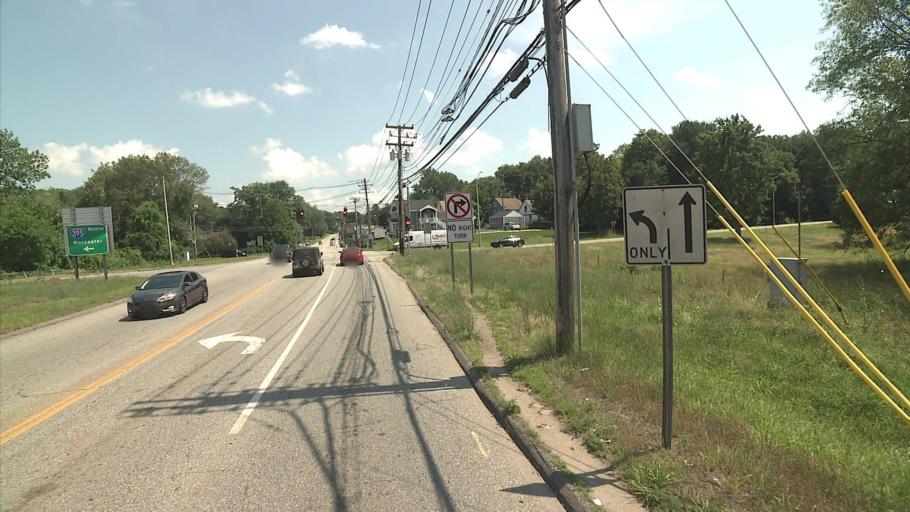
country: US
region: Connecticut
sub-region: New London County
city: Norwich
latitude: 41.5532
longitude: -72.1056
